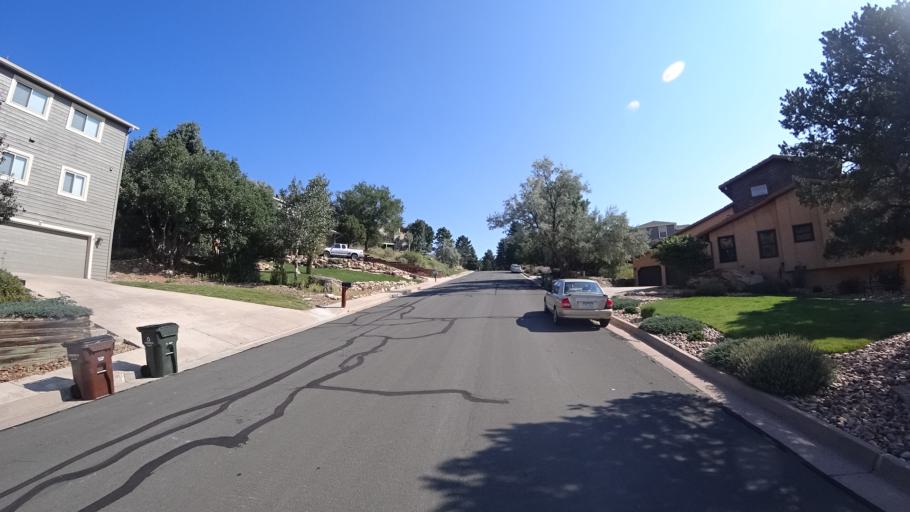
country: US
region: Colorado
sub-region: El Paso County
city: Manitou Springs
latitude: 38.9073
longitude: -104.8754
